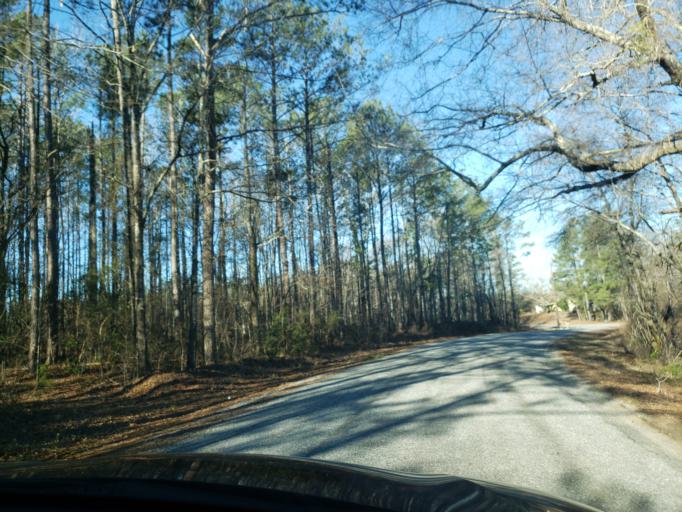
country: US
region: Alabama
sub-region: Elmore County
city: Tallassee
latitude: 32.6642
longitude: -85.8625
